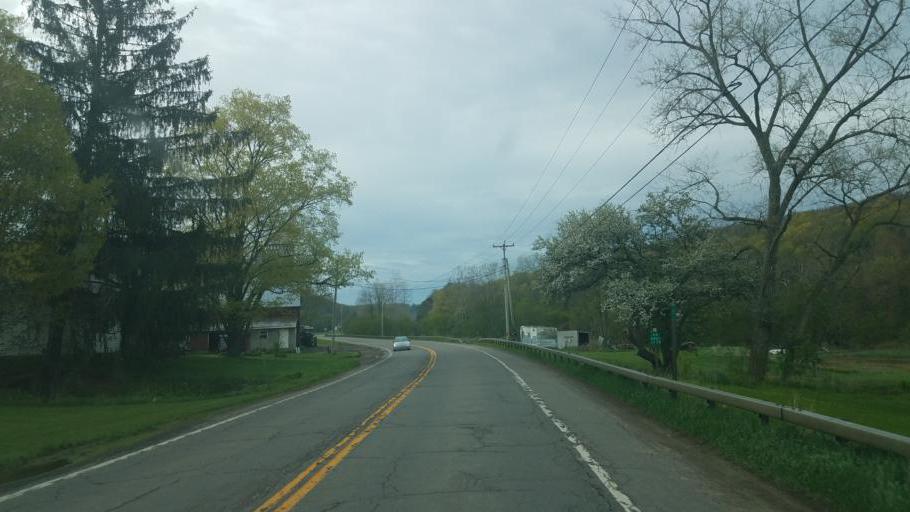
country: US
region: New York
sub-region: Steuben County
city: Canisteo
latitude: 42.2147
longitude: -77.5690
